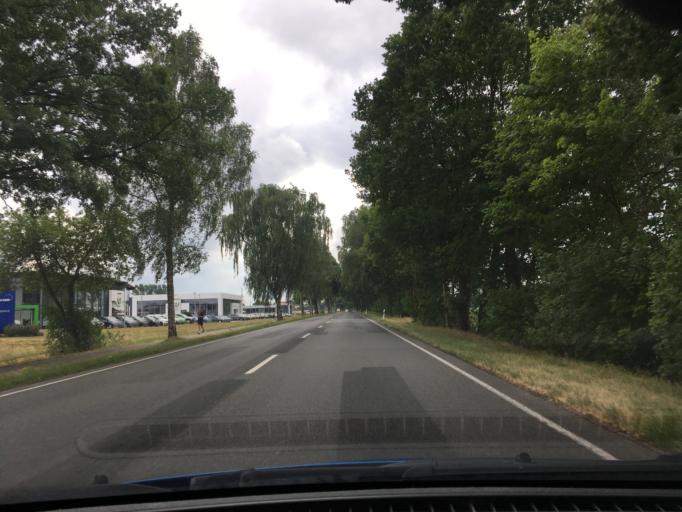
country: DE
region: Lower Saxony
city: Tostedt
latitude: 53.2910
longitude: 9.7296
